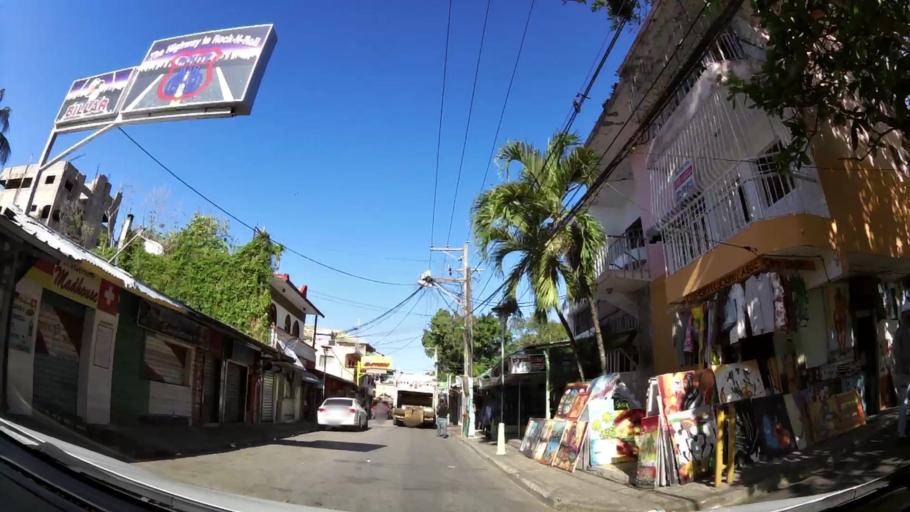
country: DO
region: Santo Domingo
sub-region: Santo Domingo
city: Boca Chica
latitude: 18.4477
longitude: -69.6078
